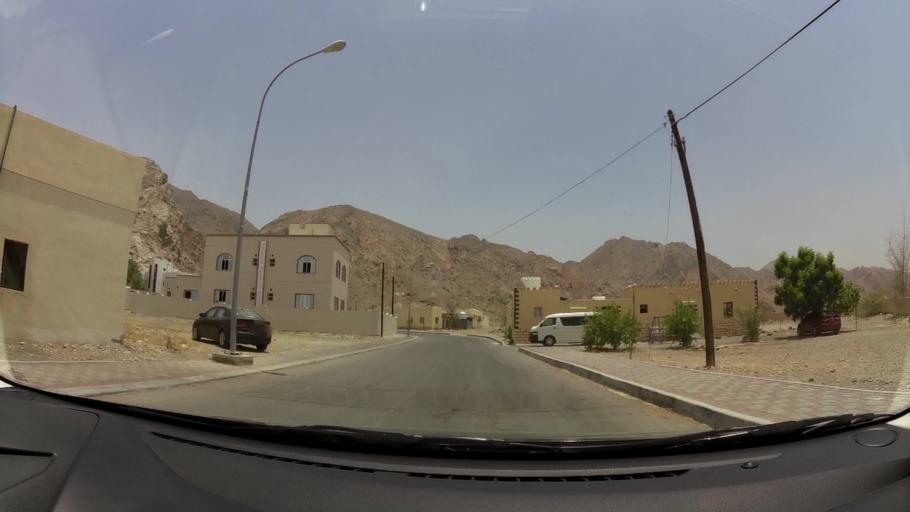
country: OM
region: Muhafazat Masqat
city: Bawshar
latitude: 23.5439
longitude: 58.4054
